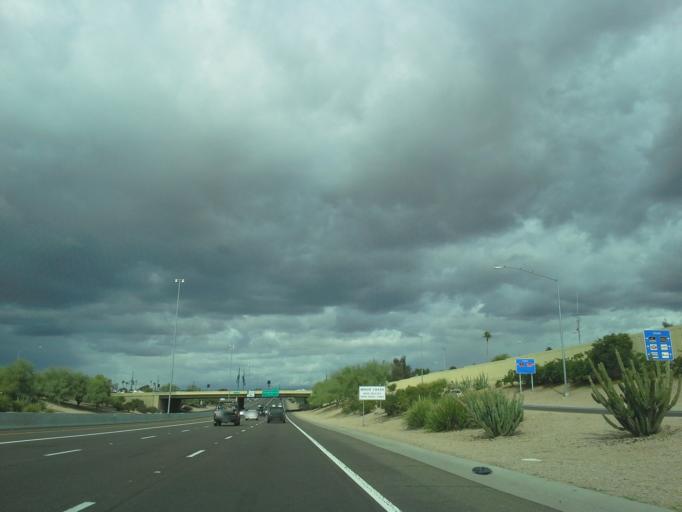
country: US
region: Arizona
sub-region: Maricopa County
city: Paradise Valley
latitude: 33.5943
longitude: -112.0093
